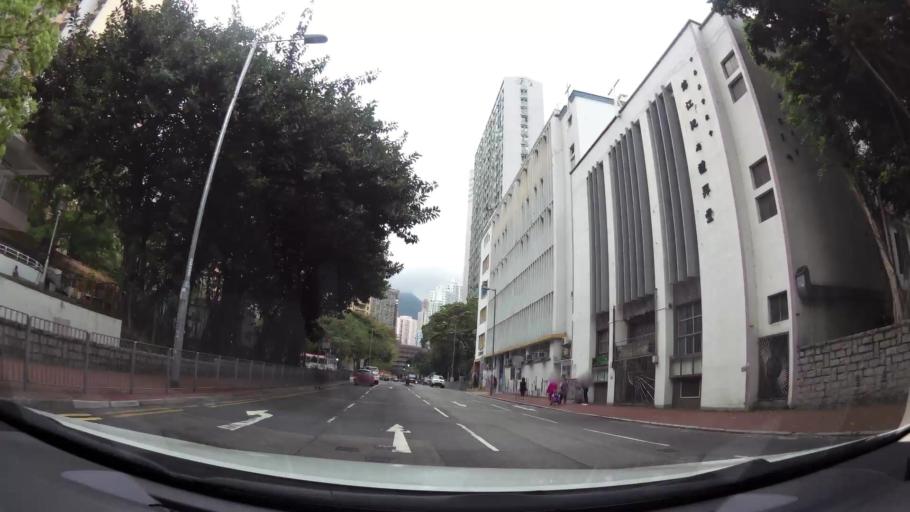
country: HK
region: Wong Tai Sin
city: Wong Tai Sin
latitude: 22.3386
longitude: 114.1932
